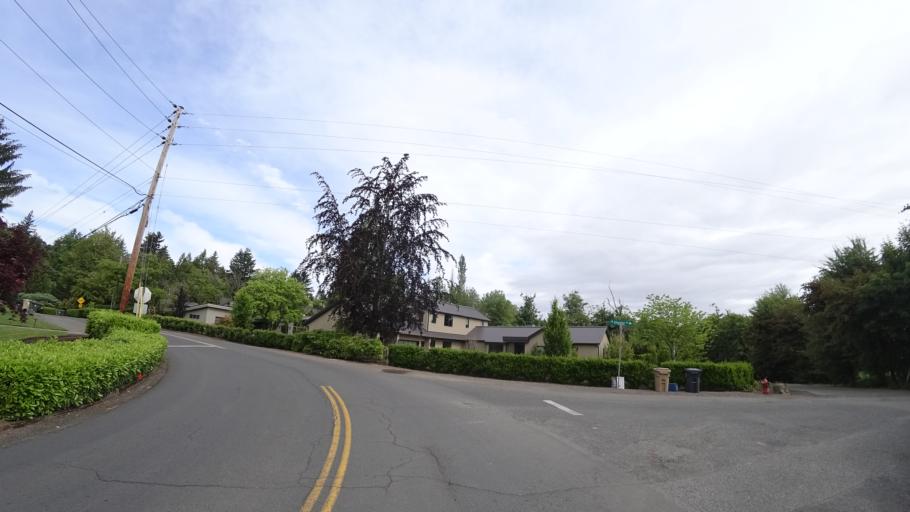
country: US
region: Oregon
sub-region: Clackamas County
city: Lake Oswego
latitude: 45.4256
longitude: -122.6889
